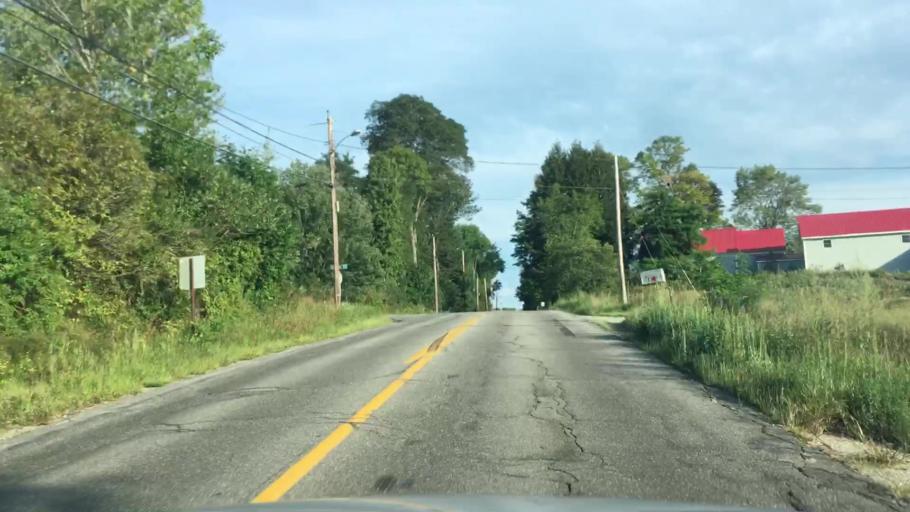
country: US
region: Maine
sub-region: Cumberland County
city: South Windham
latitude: 43.7229
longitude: -70.4014
